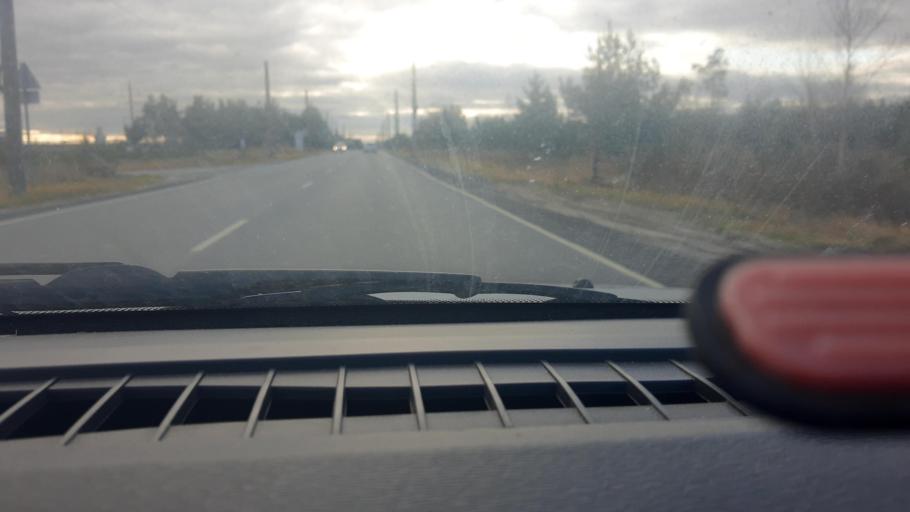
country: RU
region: Nizjnij Novgorod
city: Babino
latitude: 56.2732
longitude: 43.5506
